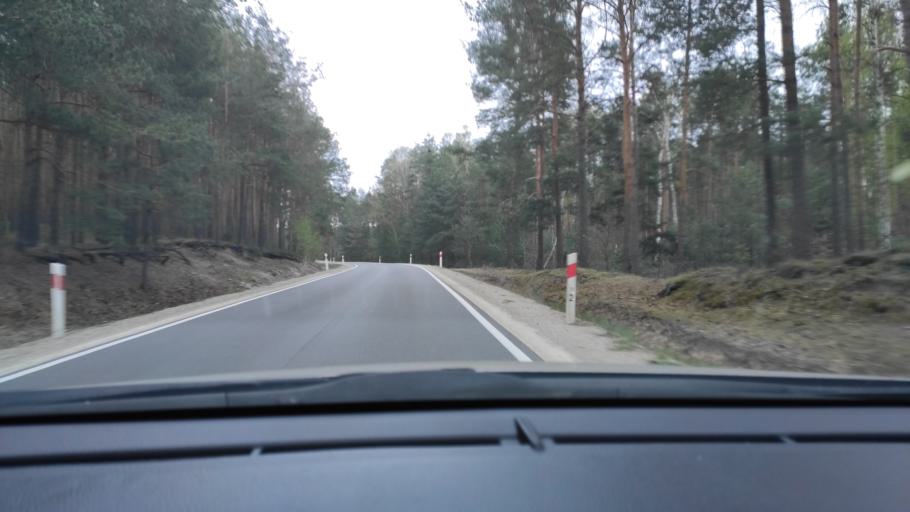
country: PL
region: Masovian Voivodeship
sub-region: Powiat zwolenski
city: Zwolen
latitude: 51.4092
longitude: 21.5192
